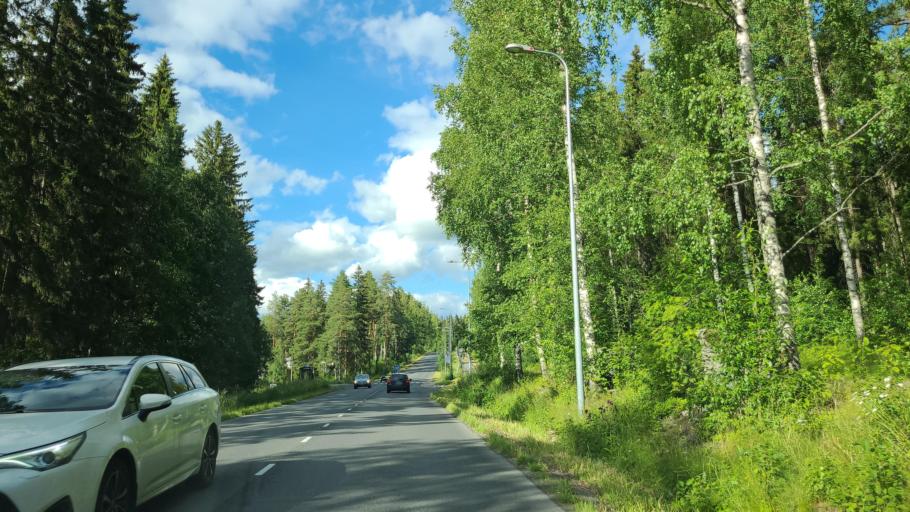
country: FI
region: Northern Savo
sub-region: Kuopio
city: Kuopio
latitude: 62.9355
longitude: 27.6343
